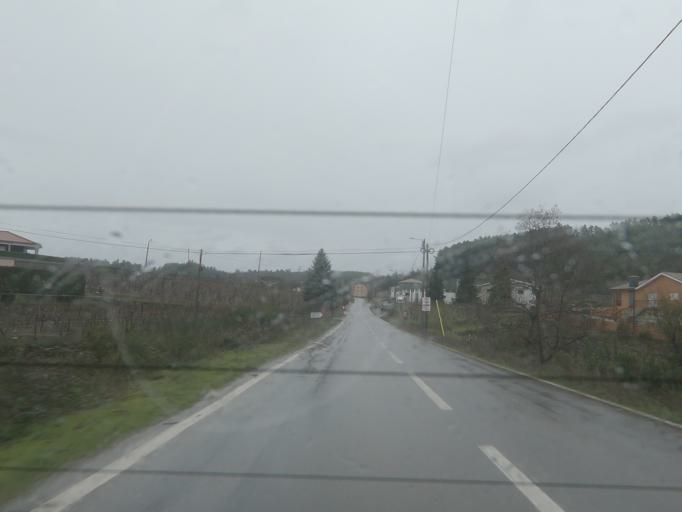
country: PT
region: Vila Real
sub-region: Sabrosa
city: Vilela
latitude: 41.2173
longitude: -7.6745
